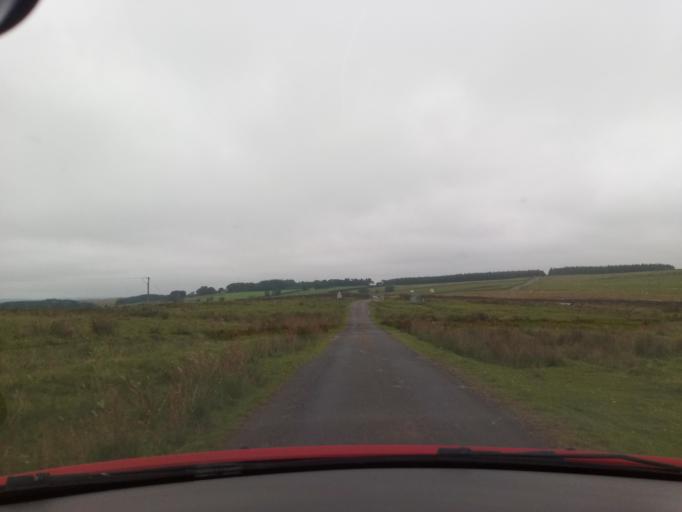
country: GB
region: England
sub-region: Northumberland
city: Otterburn
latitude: 55.2549
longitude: -2.1073
